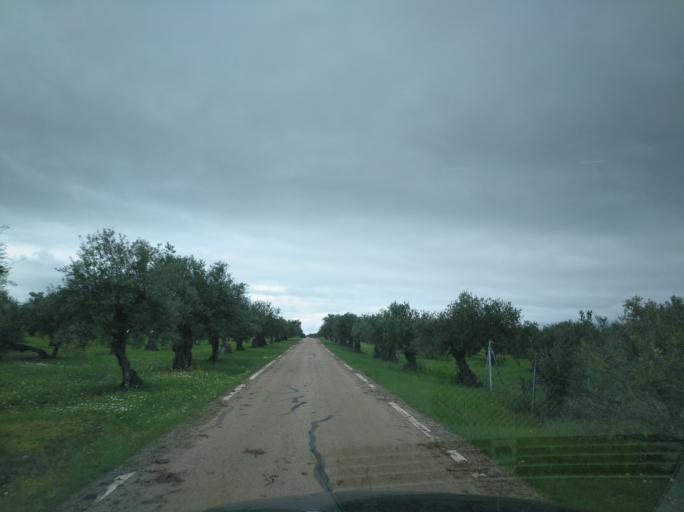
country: PT
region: Portalegre
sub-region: Campo Maior
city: Campo Maior
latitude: 38.9824
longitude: -7.0346
